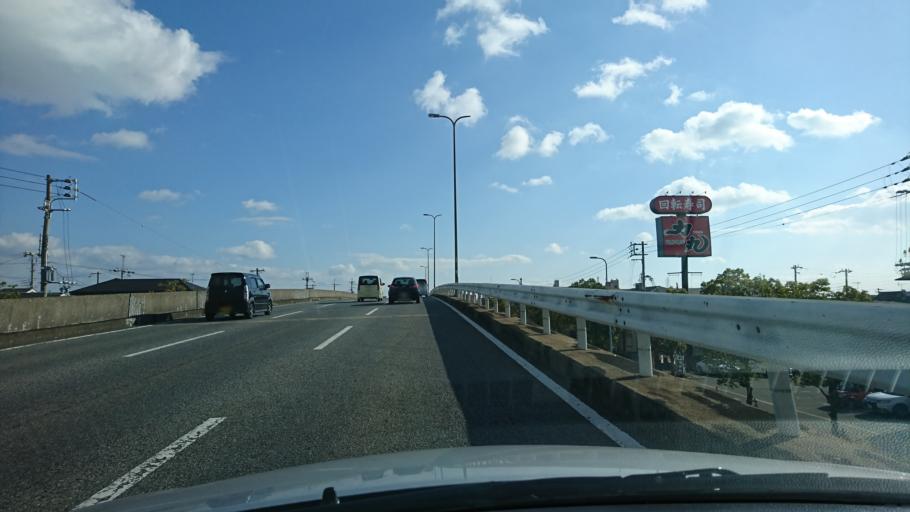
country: JP
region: Hyogo
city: Kakogawacho-honmachi
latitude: 34.7400
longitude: 134.8458
